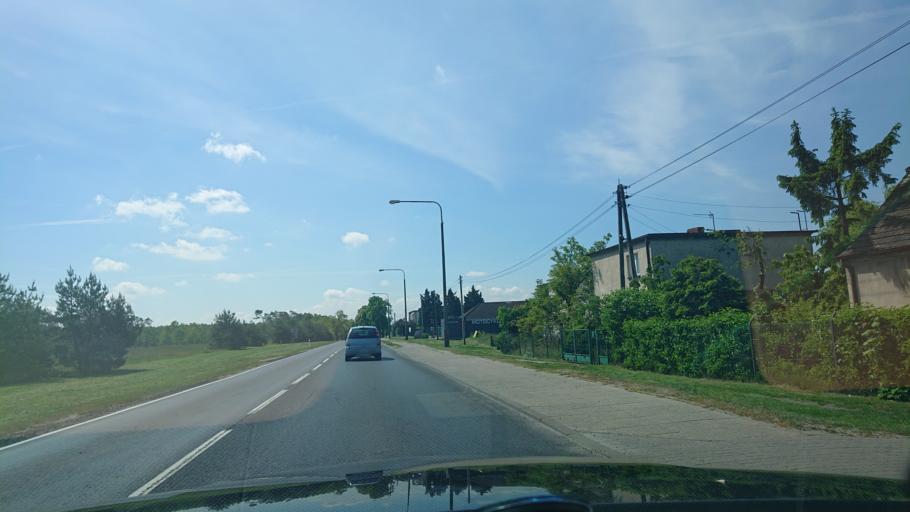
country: PL
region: Greater Poland Voivodeship
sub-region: Powiat gnieznienski
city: Gniezno
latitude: 52.5097
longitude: 17.5949
